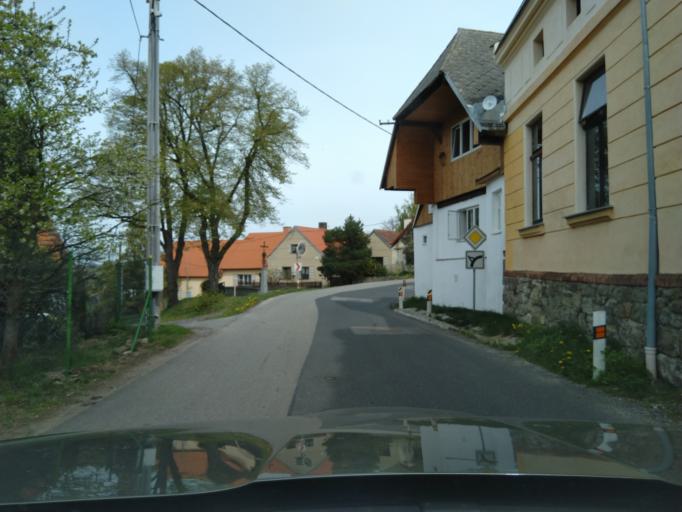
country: CZ
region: Jihocesky
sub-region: Okres Prachatice
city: Stachy
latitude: 49.1796
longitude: 13.6408
